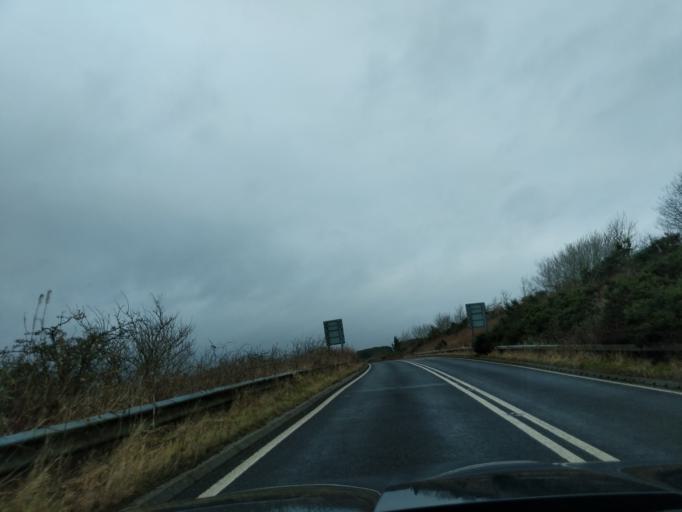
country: GB
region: England
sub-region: Northumberland
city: Rothley
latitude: 55.1605
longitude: -2.0156
